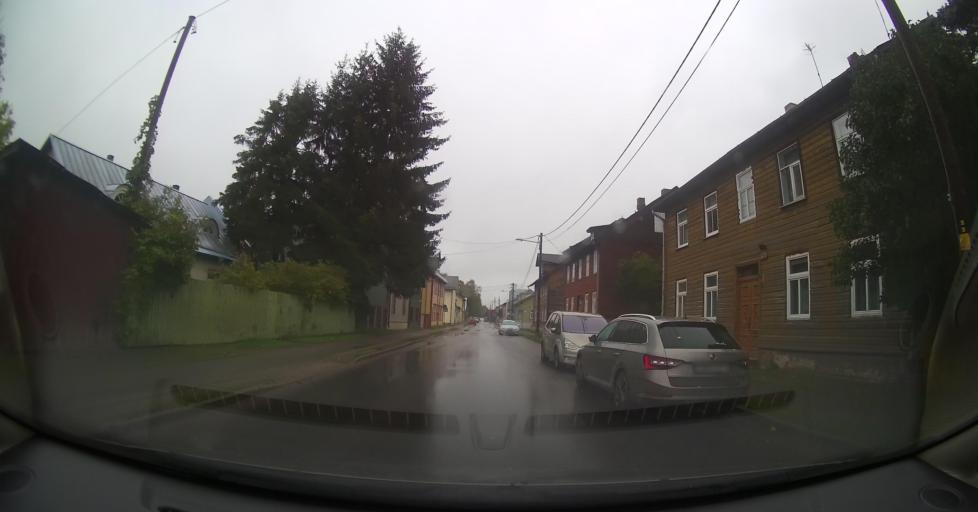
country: EE
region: Tartu
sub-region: Tartu linn
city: Tartu
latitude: 58.3863
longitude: 26.7140
